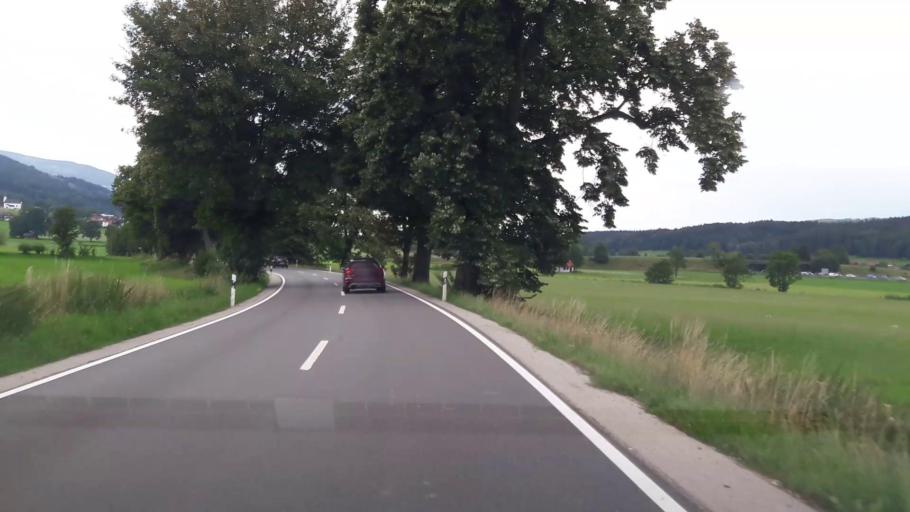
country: DE
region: Bavaria
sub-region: Upper Bavaria
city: Piding
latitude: 47.7739
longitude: 12.8821
